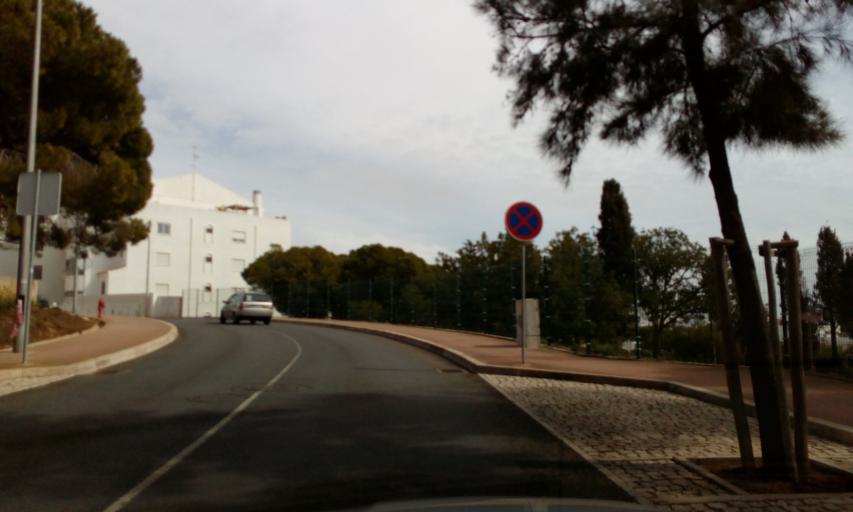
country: PT
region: Faro
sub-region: Albufeira
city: Albufeira
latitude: 37.0880
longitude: -8.2447
